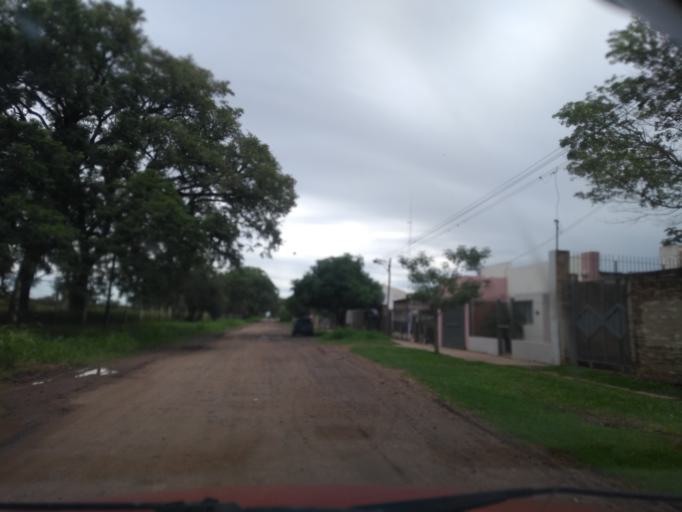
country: AR
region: Chaco
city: Barranqueras
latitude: -27.4790
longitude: -58.9604
